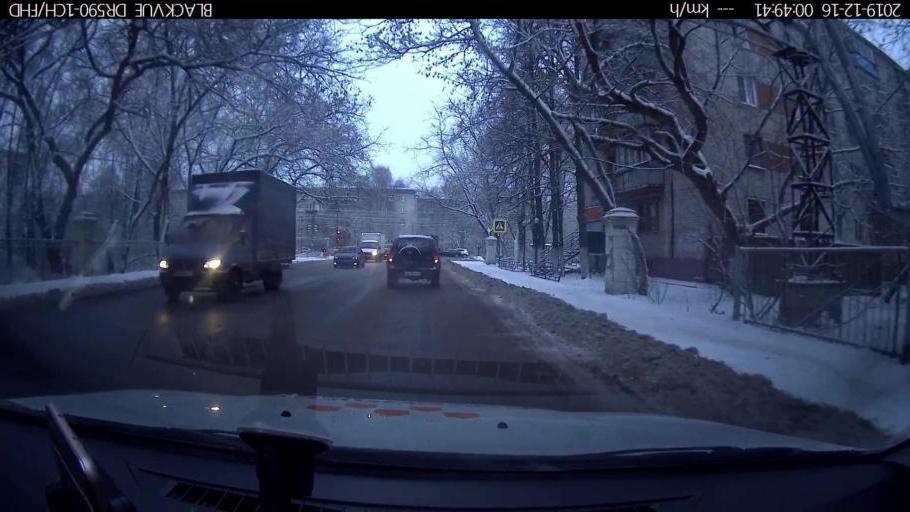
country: RU
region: Nizjnij Novgorod
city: Gorbatovka
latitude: 56.3122
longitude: 43.8580
